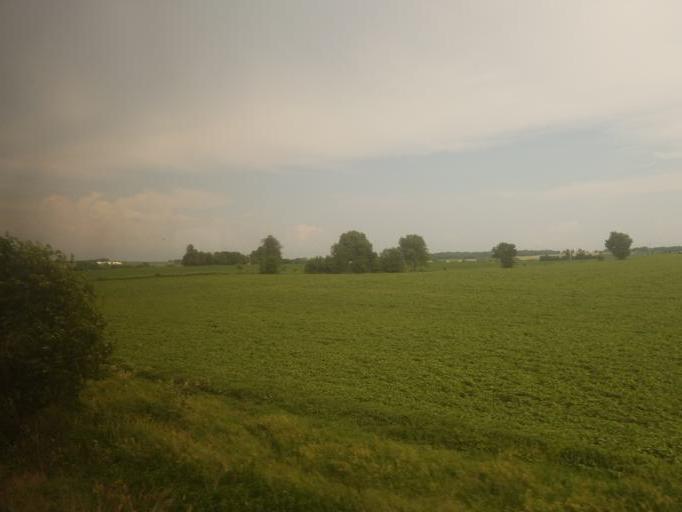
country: US
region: Illinois
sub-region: Henry County
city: Kewanee
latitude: 41.3031
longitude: -89.7278
